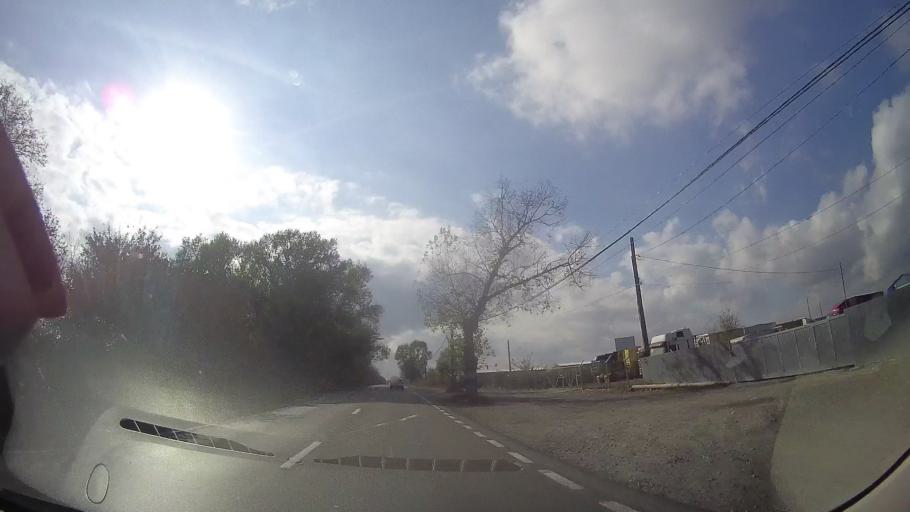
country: RO
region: Constanta
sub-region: Comuna Agigea
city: Agigea
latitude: 44.0847
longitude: 28.6070
